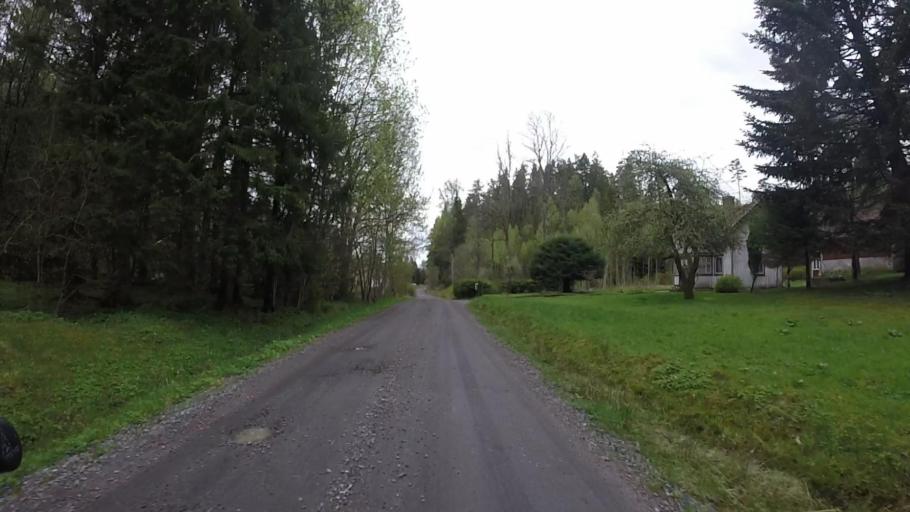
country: SE
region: Vaestra Goetaland
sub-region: Trollhattan
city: Sjuntorp
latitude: 58.2083
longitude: 12.2114
